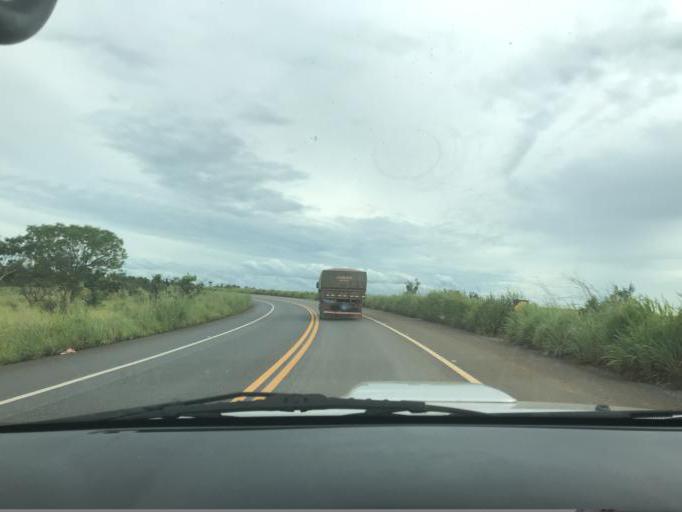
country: BR
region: Minas Gerais
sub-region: Araxa
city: Araxa
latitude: -19.3838
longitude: -46.8603
